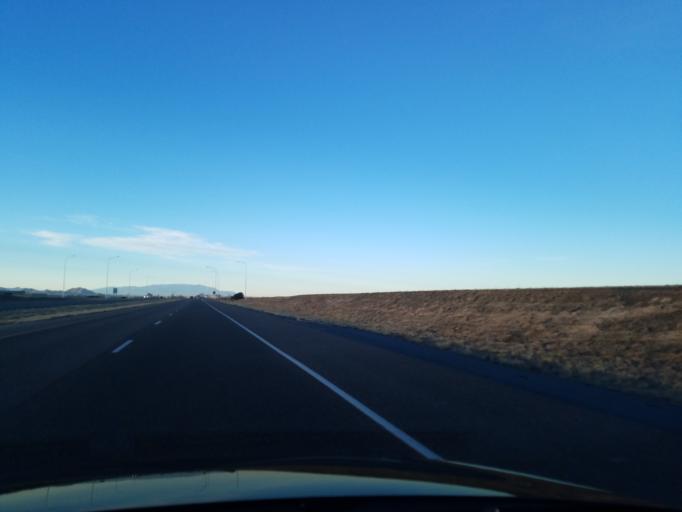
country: US
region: New Mexico
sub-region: Santa Fe County
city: Agua Fria
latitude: 35.6587
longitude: -106.0368
